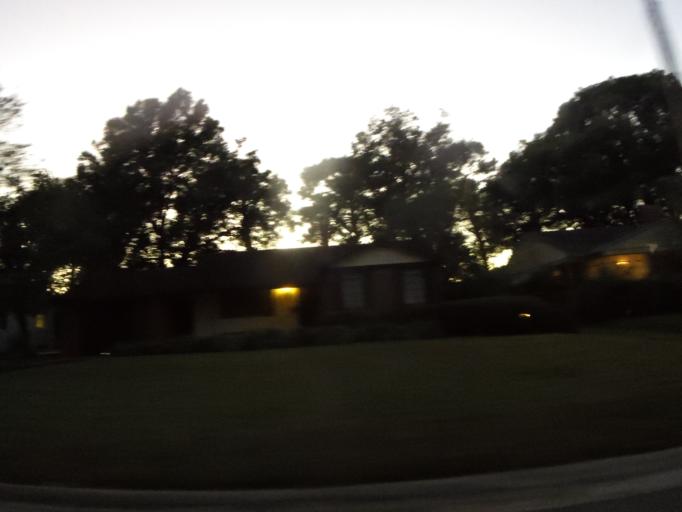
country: US
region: Florida
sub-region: Duval County
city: Jacksonville
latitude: 30.2880
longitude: -81.7127
